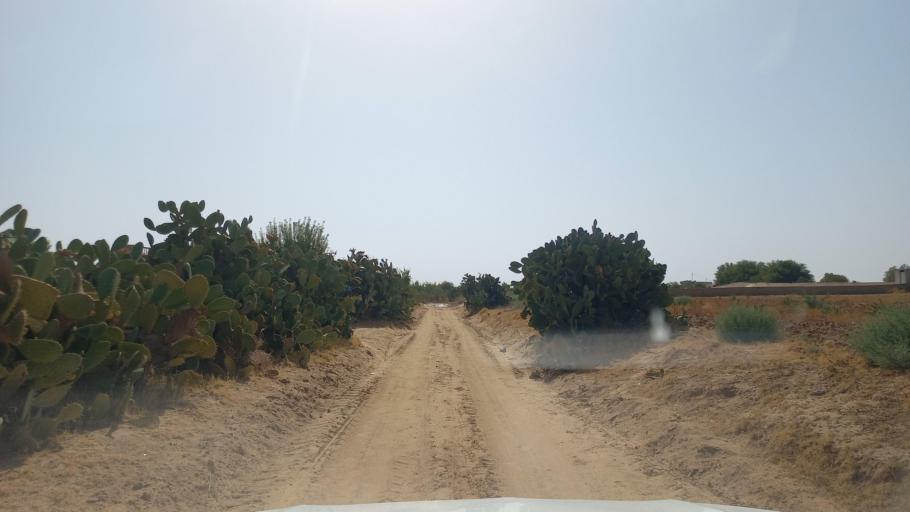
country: TN
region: Al Qasrayn
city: Kasserine
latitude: 35.2440
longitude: 9.0449
